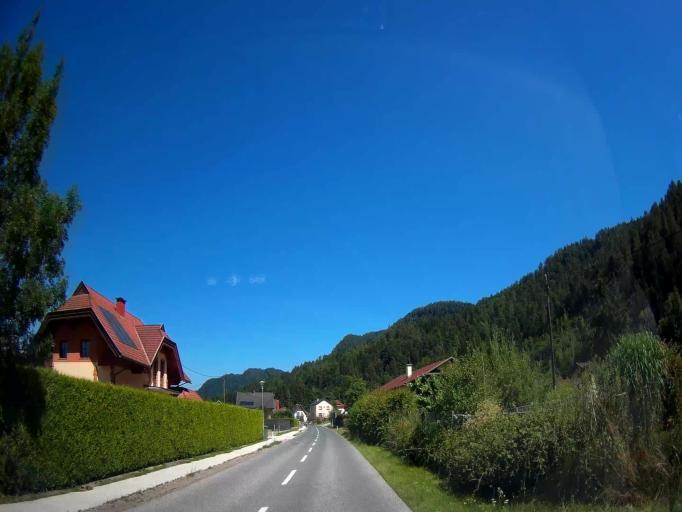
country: AT
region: Carinthia
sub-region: Politischer Bezirk Klagenfurt Land
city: Ebenthal
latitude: 46.6037
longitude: 14.4082
